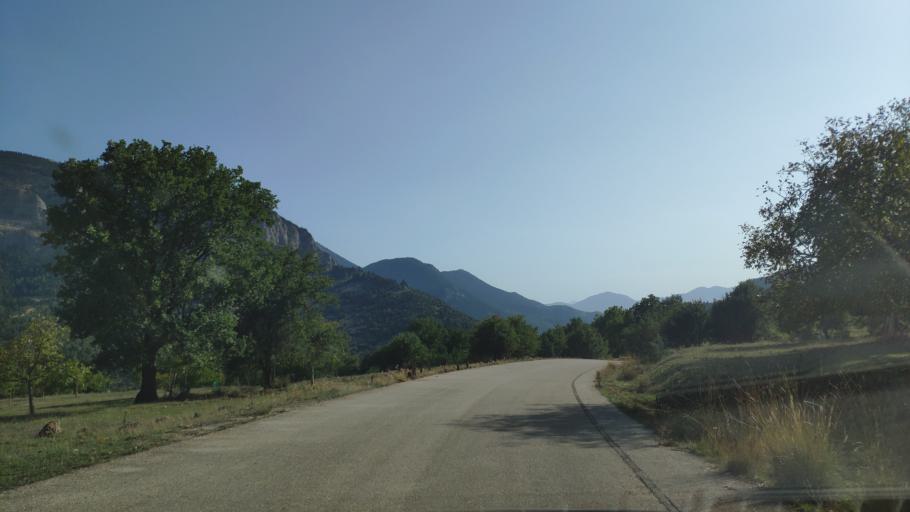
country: GR
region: West Greece
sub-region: Nomos Achaias
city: Aiyira
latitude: 37.9925
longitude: 22.3571
